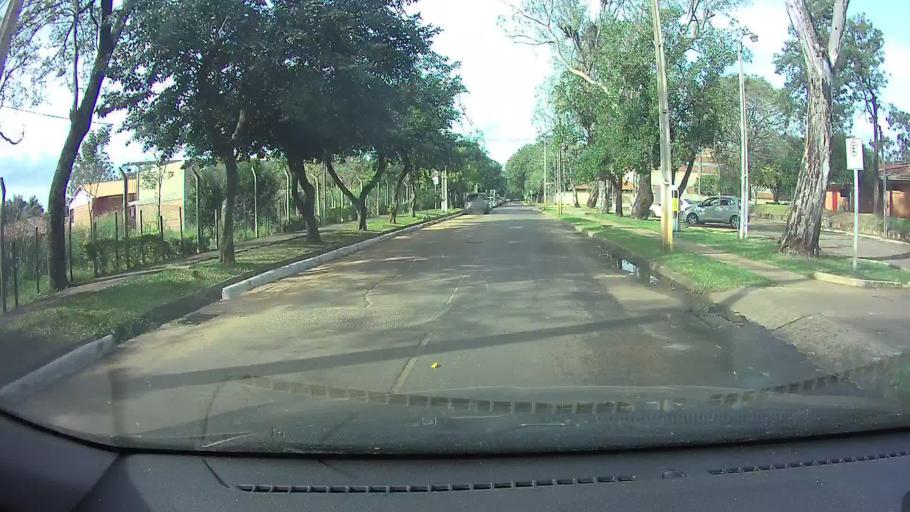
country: PY
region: Central
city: Fernando de la Mora
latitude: -25.3316
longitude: -57.5187
